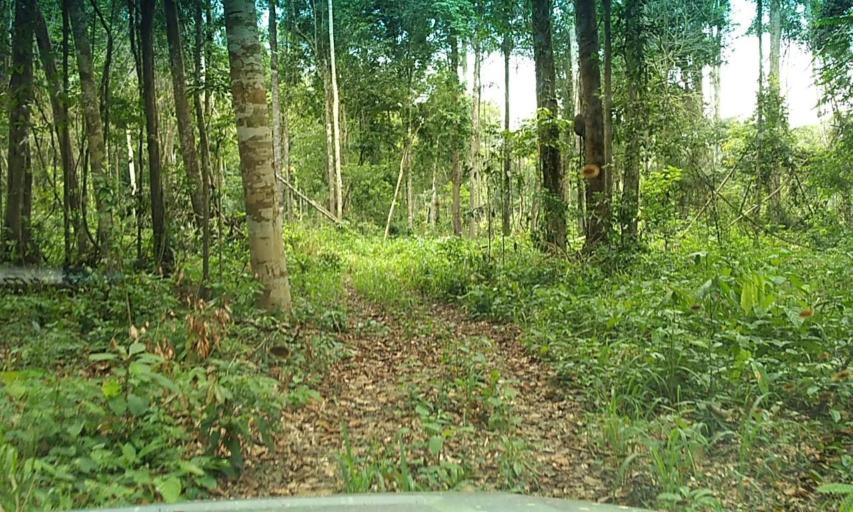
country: BR
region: Para
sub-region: Senador Jose Porfirio
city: Senador Jose Porfirio
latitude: -2.7301
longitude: -51.7319
